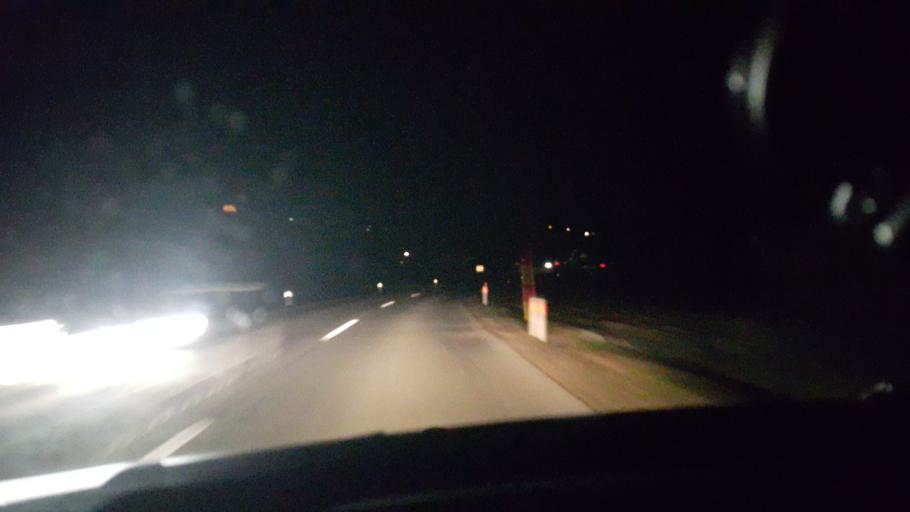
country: SI
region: Majsperk
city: Majsperk
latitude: 46.3654
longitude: 15.7646
